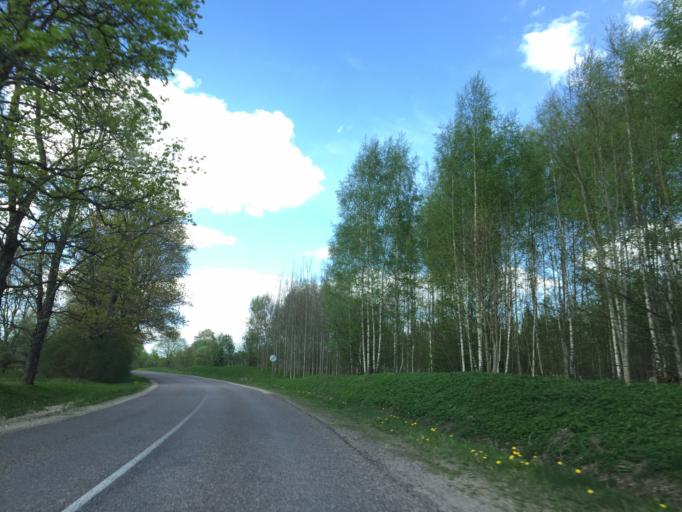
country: LV
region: Limbazu Rajons
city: Limbazi
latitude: 57.4767
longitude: 24.7113
